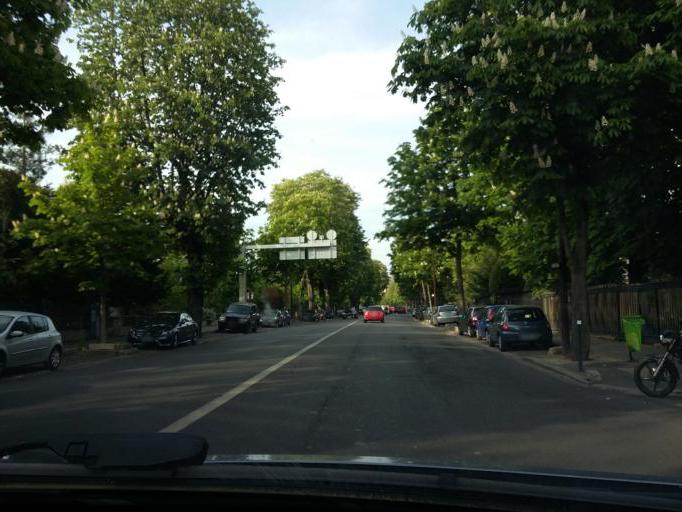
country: FR
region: Ile-de-France
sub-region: Departement des Hauts-de-Seine
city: Puteaux
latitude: 48.8785
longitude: 2.2487
